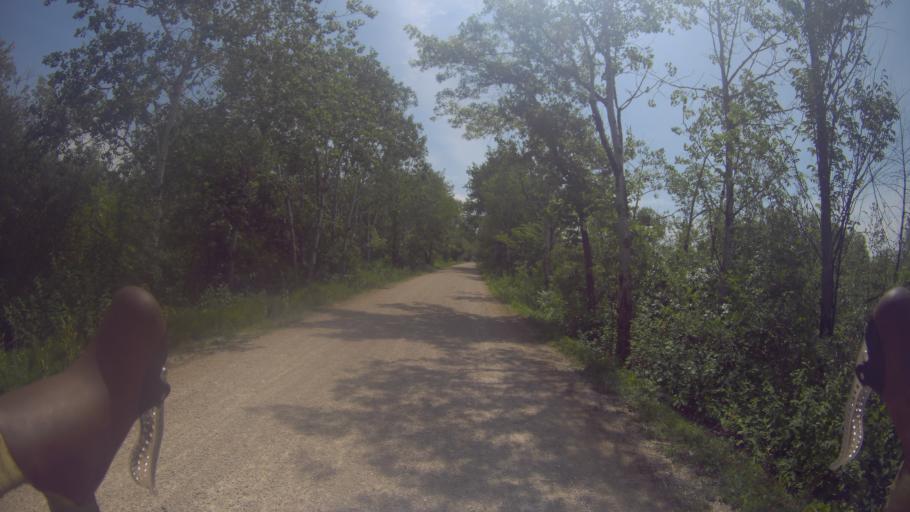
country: US
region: Wisconsin
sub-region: Jefferson County
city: Lake Mills
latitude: 43.0683
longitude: -88.9376
